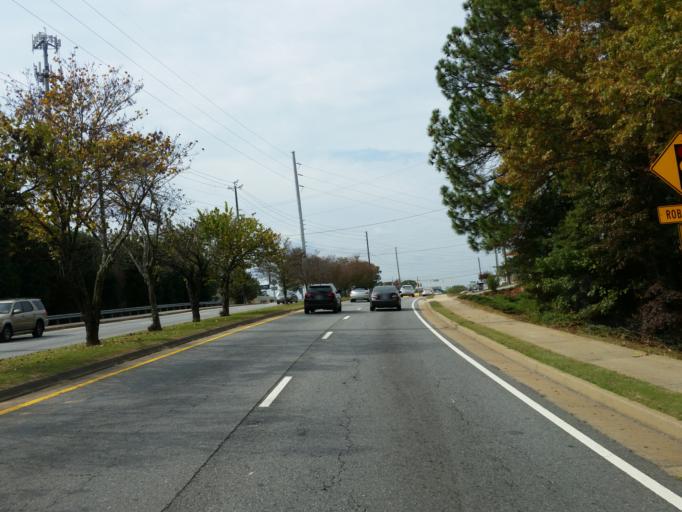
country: US
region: Georgia
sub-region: Fulton County
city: Sandy Springs
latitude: 33.9780
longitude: -84.4383
